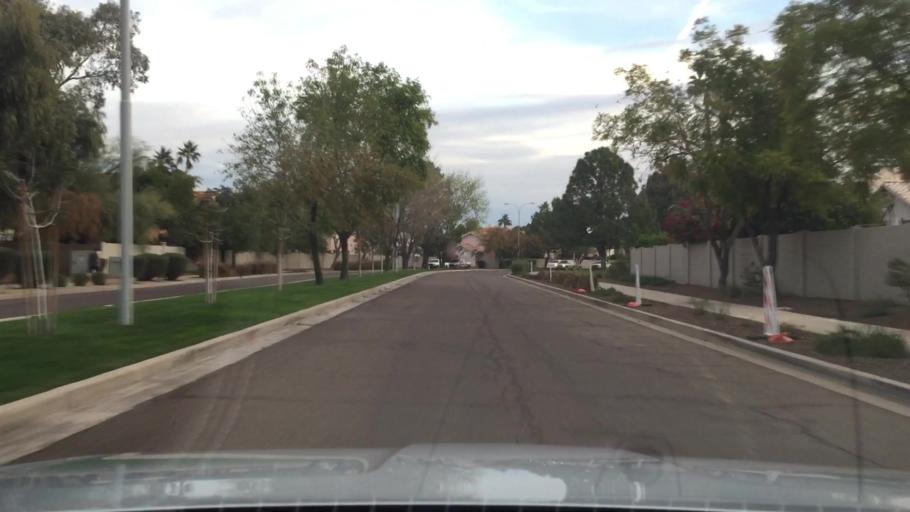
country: US
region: Arizona
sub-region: Maricopa County
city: Gilbert
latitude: 33.3766
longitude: -111.7924
